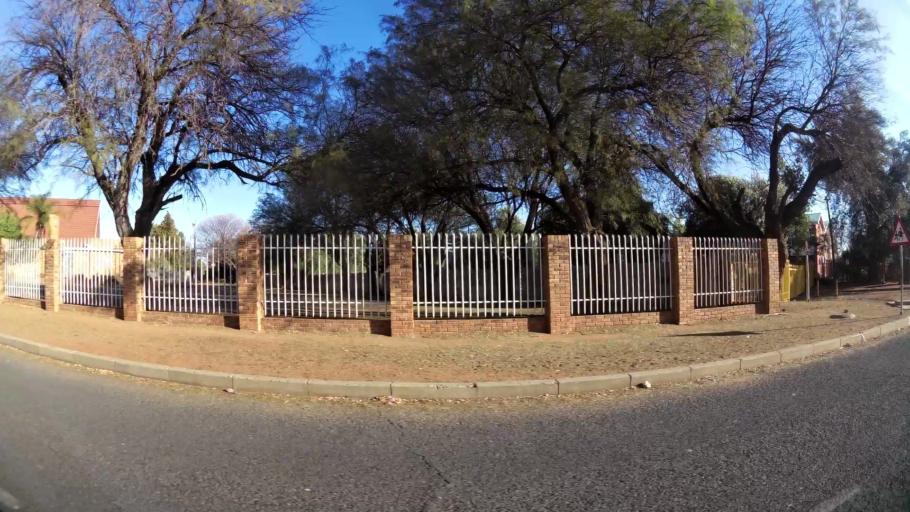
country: ZA
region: Northern Cape
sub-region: Frances Baard District Municipality
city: Kimberley
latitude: -28.7380
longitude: 24.7373
